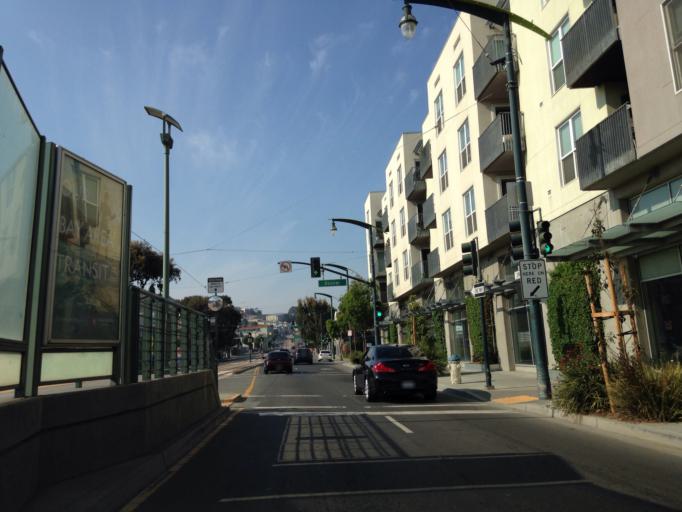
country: US
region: California
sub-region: San Mateo County
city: Brisbane
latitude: 37.7250
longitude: -122.3946
